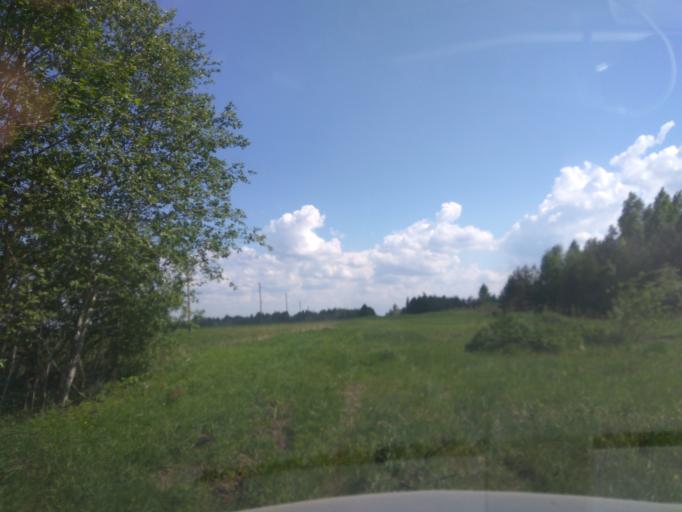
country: LV
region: Kuldigas Rajons
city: Kuldiga
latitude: 57.1785
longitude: 22.0073
